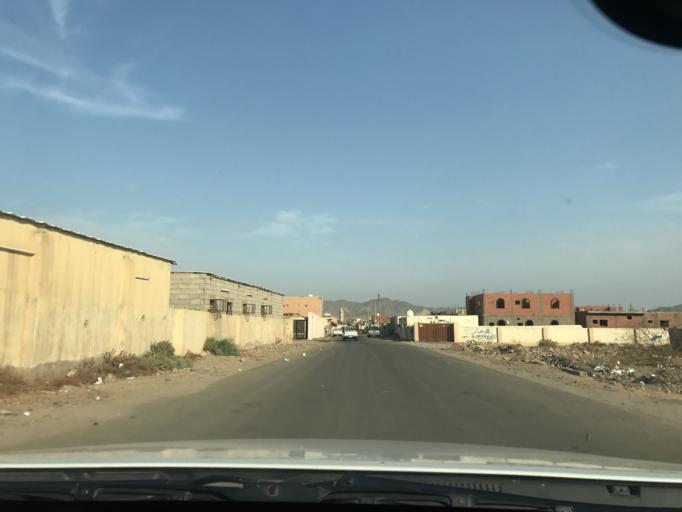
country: SA
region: Makkah
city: Al Jumum
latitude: 21.4430
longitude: 39.5187
